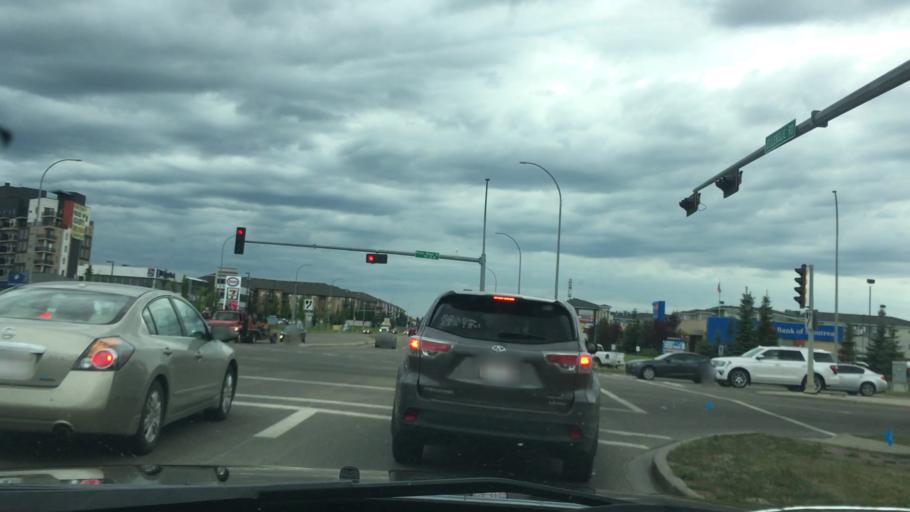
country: CA
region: Alberta
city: Beaumont
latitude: 53.4250
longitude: -113.5161
